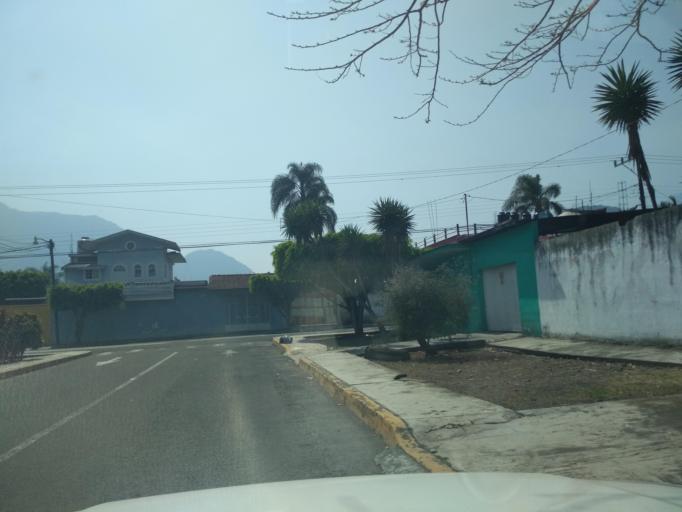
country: MX
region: Veracruz
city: Orizaba
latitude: 18.8403
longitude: -97.0953
